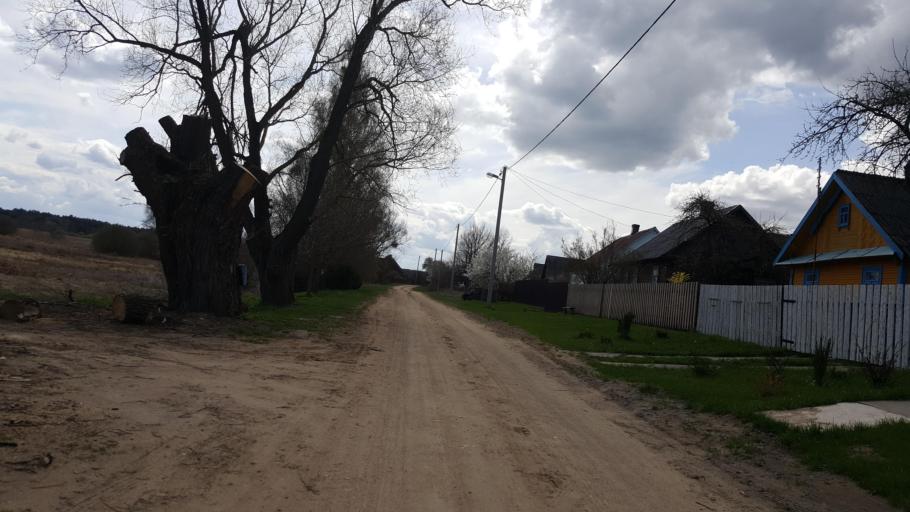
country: BY
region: Brest
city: Kamyanyets
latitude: 52.3525
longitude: 23.7324
